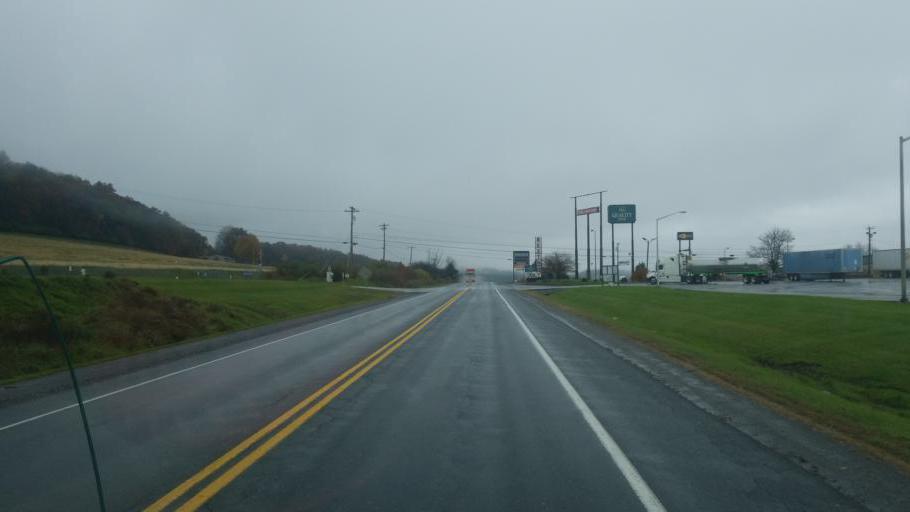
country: US
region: Pennsylvania
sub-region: Centre County
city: Milesburg
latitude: 40.9600
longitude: -77.7628
